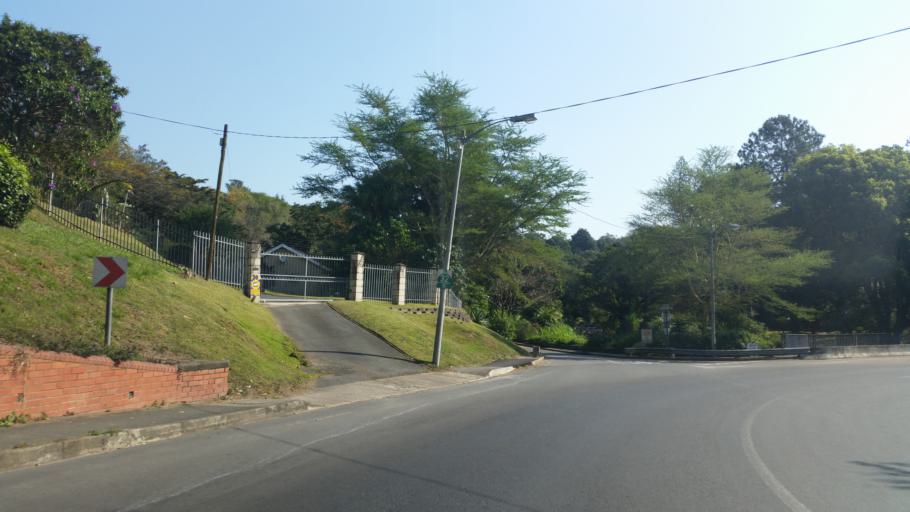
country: ZA
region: KwaZulu-Natal
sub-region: eThekwini Metropolitan Municipality
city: Berea
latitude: -29.8310
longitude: 30.9109
